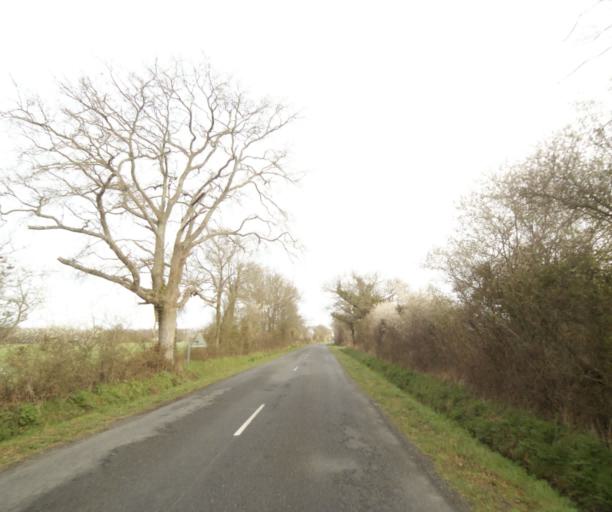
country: FR
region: Pays de la Loire
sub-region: Departement de la Loire-Atlantique
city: Bouvron
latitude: 47.3992
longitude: -1.8840
